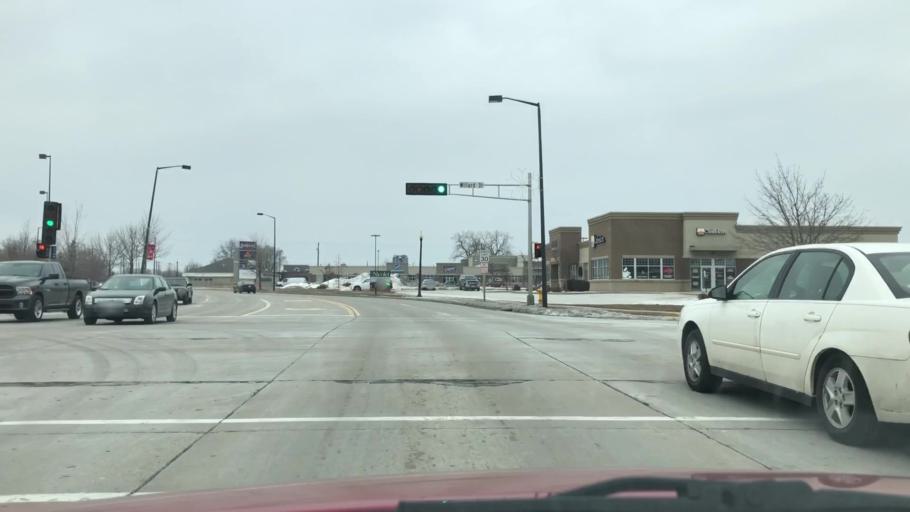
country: US
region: Wisconsin
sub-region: Brown County
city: Ashwaubenon
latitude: 44.4851
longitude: -88.0608
